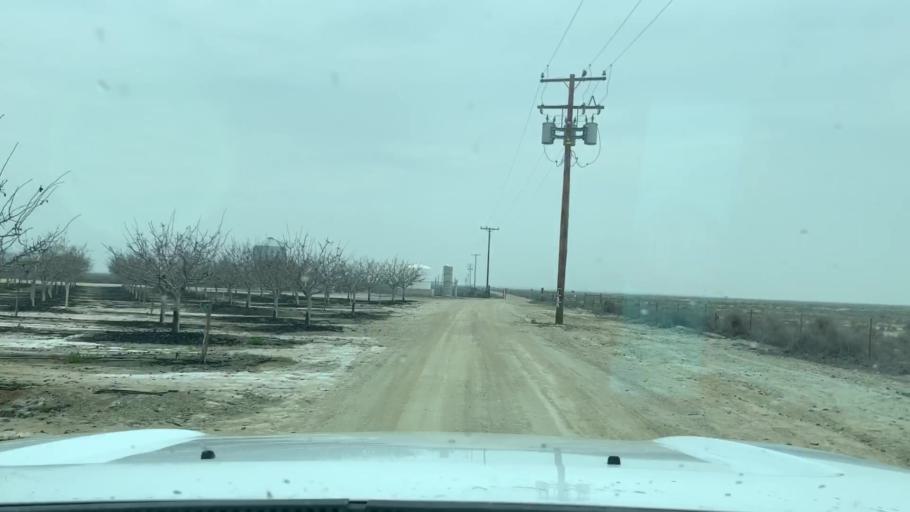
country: US
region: California
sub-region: Tulare County
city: Earlimart
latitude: 35.8401
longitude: -119.3398
